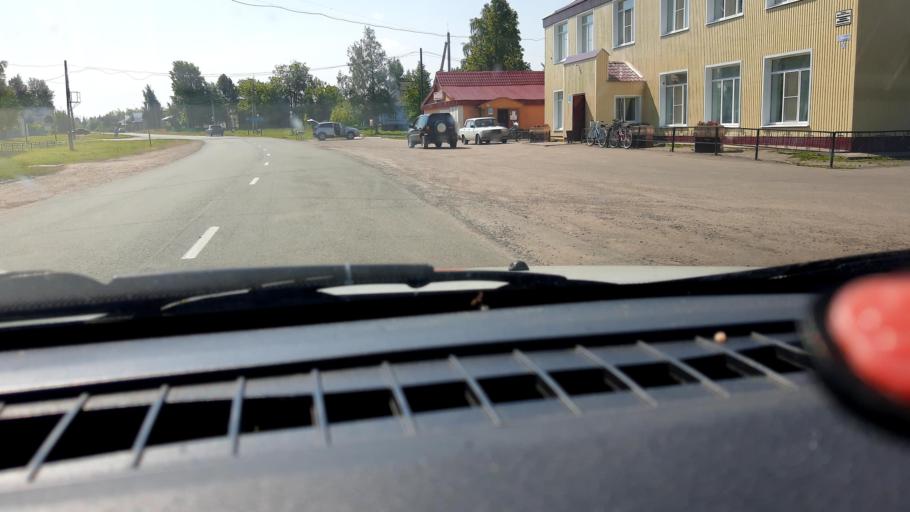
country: RU
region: Nizjnij Novgorod
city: Sharanga
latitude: 57.0512
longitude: 46.5457
